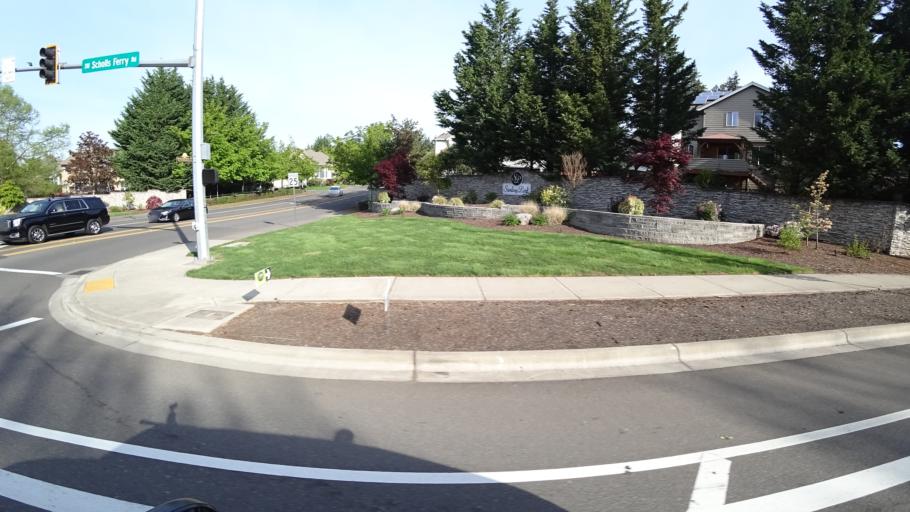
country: US
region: Oregon
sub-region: Washington County
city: King City
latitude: 45.4322
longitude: -122.8397
